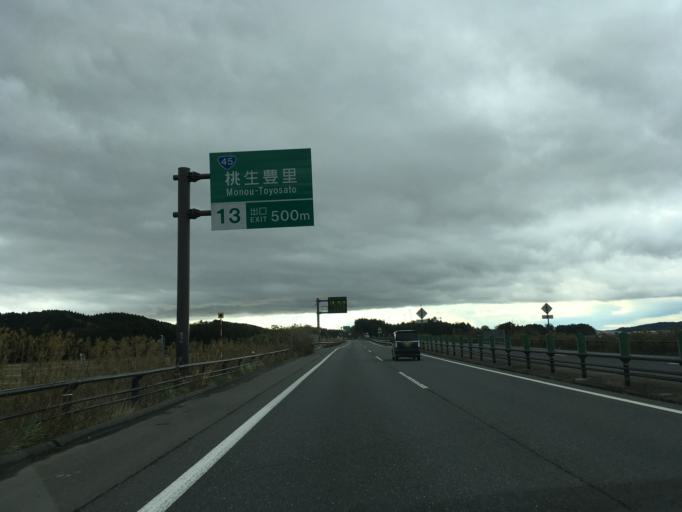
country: JP
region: Miyagi
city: Wakuya
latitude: 38.5660
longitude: 141.2726
